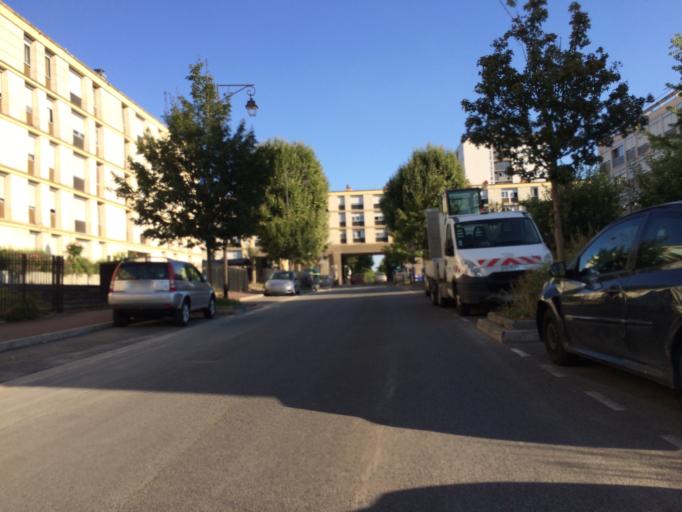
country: FR
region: Ile-de-France
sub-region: Departement de l'Essonne
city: Massy
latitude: 48.7356
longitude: 2.2849
